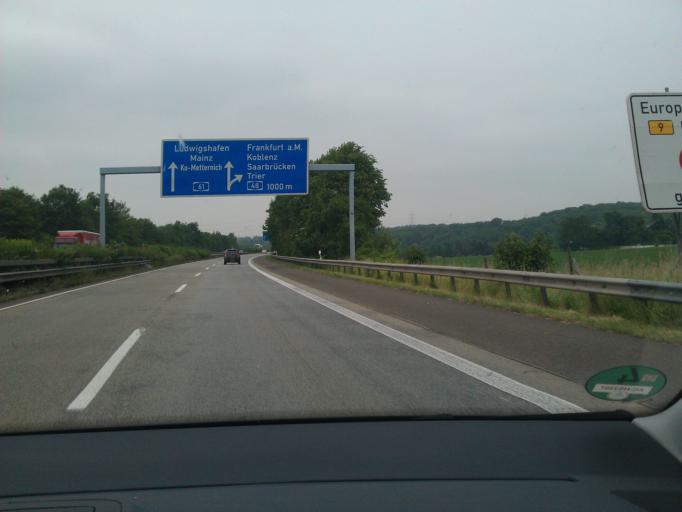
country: DE
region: Rheinland-Pfalz
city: Bassenheim
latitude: 50.3668
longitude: 7.4620
